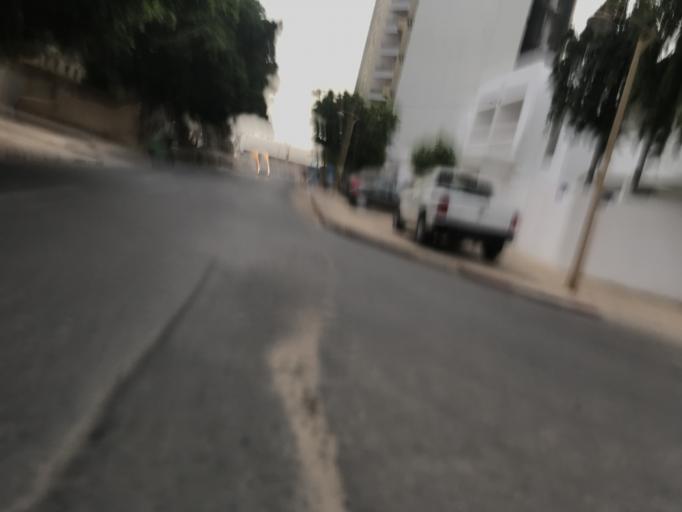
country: SN
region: Dakar
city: Dakar
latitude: 14.6636
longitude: -17.4406
